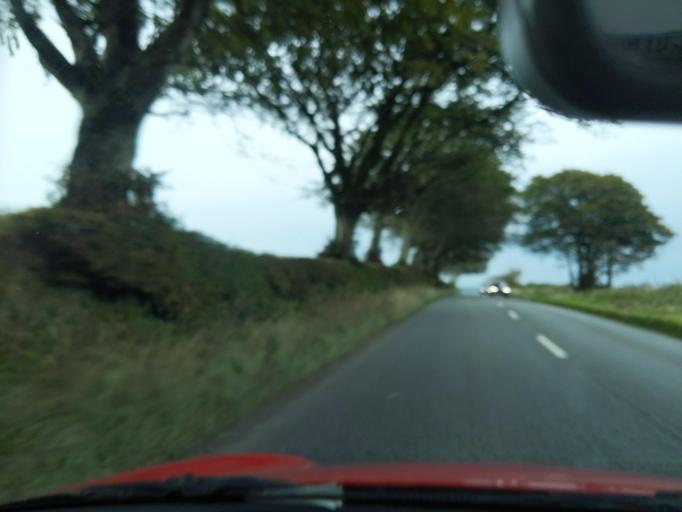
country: GB
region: England
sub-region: Devon
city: Okehampton
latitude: 50.7219
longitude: -4.0512
